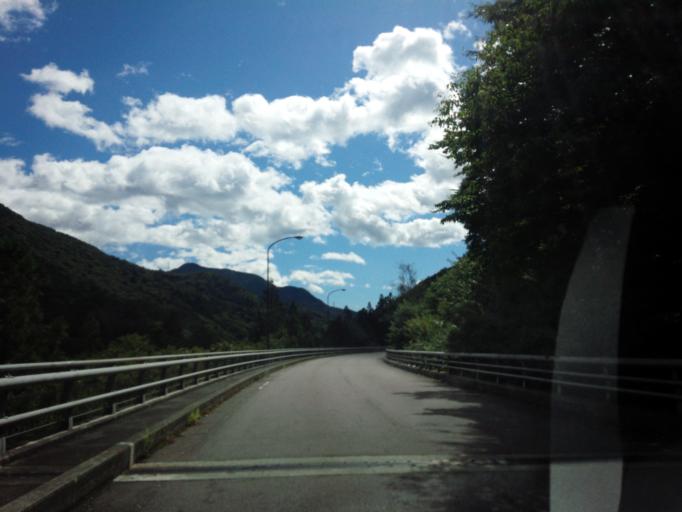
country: JP
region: Gunma
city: Nakanojomachi
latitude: 36.6854
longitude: 138.7738
